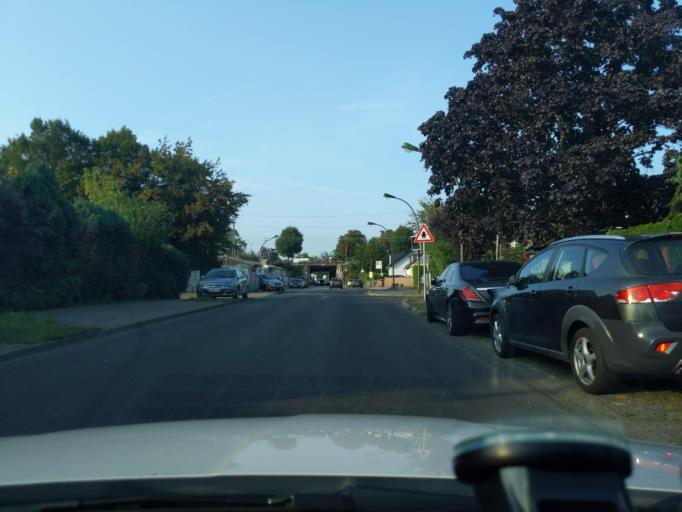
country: DE
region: North Rhine-Westphalia
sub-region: Regierungsbezirk Dusseldorf
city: Dusseldorf
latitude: 51.2063
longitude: 6.8147
